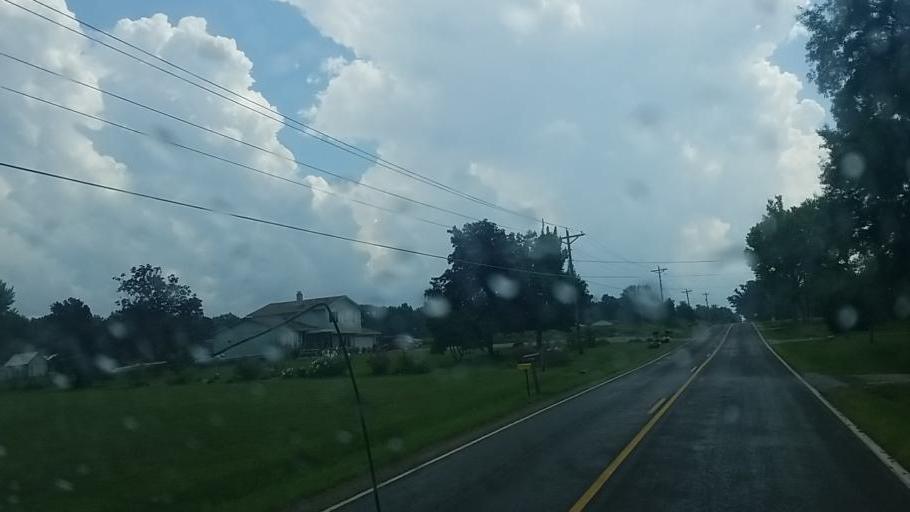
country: US
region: Ohio
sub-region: Lorain County
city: Grafton
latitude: 41.1634
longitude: -82.0036
